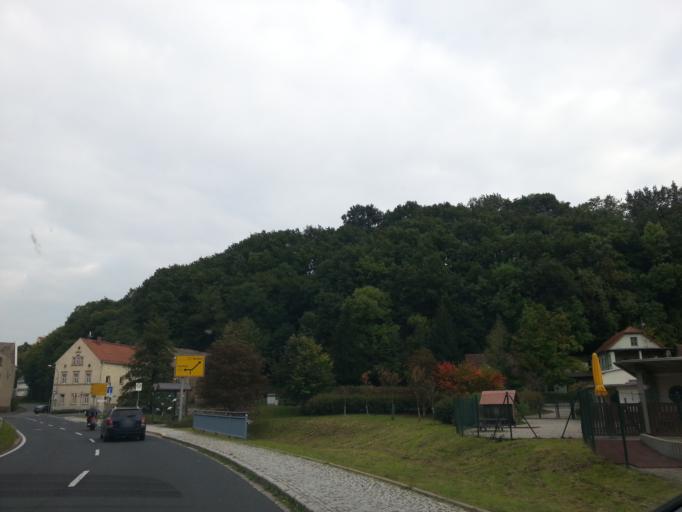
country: DE
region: Saxony
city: Meissen
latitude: 51.1967
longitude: 13.4044
